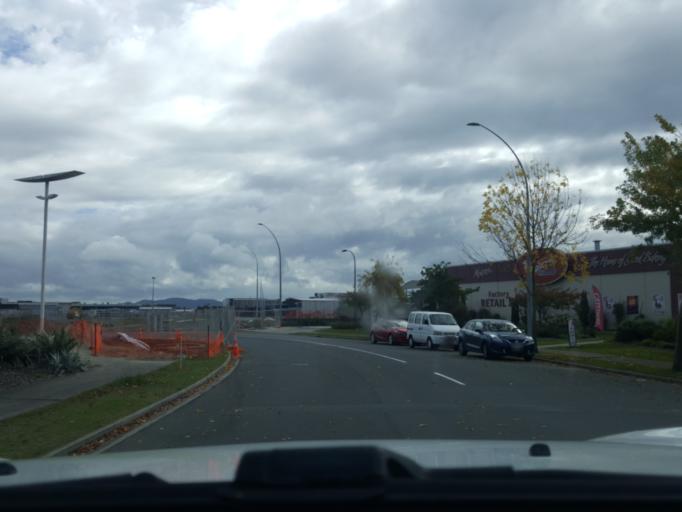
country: NZ
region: Waikato
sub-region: Hamilton City
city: Hamilton
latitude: -37.7459
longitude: 175.2350
